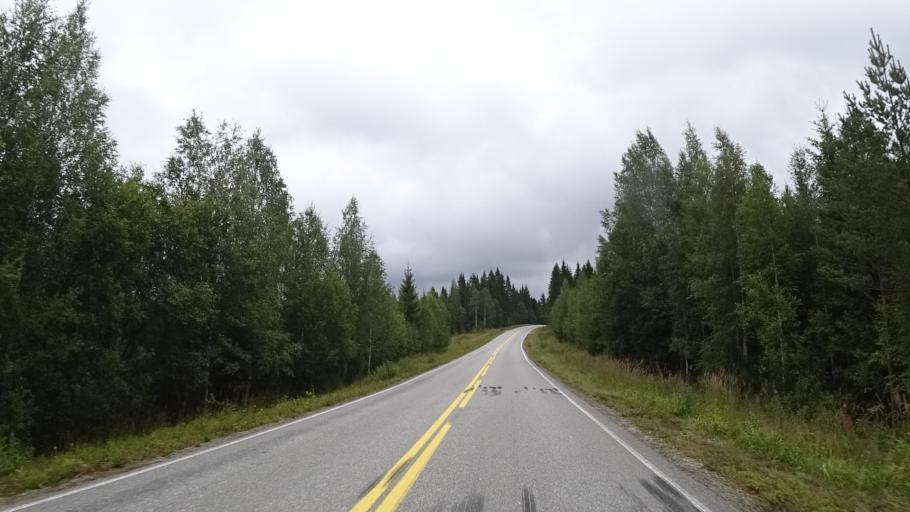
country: FI
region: North Karelia
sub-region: Joensuu
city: Ilomantsi
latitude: 63.2605
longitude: 30.6750
